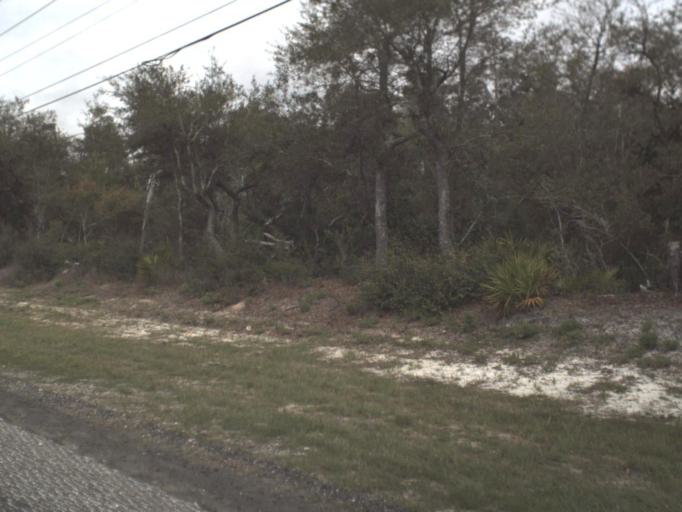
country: US
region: Florida
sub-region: Santa Rosa County
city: Navarre
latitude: 30.4019
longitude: -86.8921
